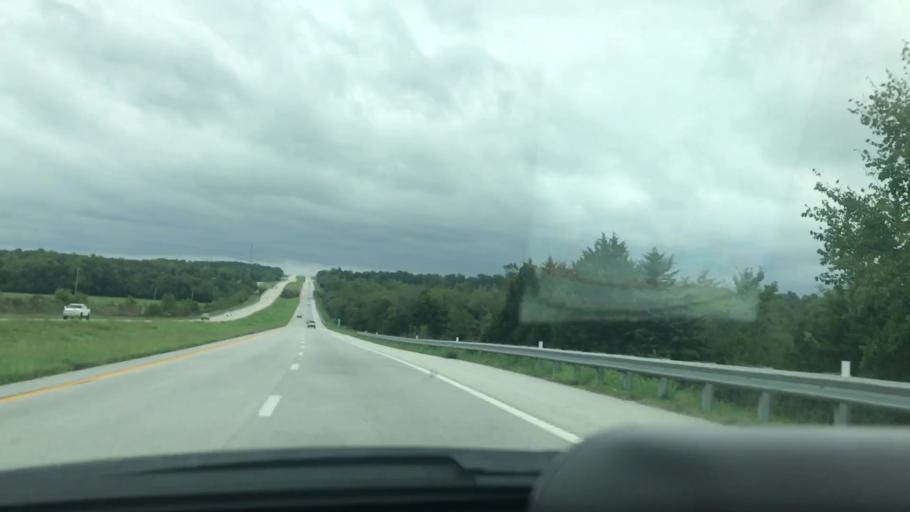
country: US
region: Missouri
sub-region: Greene County
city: Fair Grove
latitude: 37.4101
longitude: -93.1456
